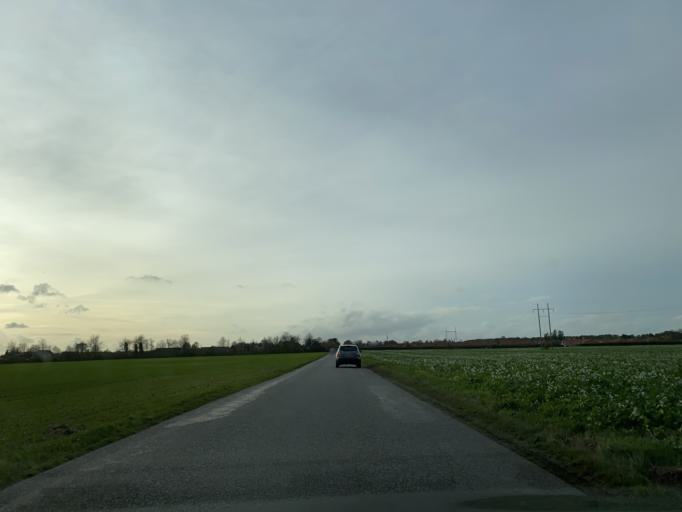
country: DK
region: Central Jutland
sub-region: Skanderborg Kommune
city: Skovby
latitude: 56.1595
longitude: 9.9643
